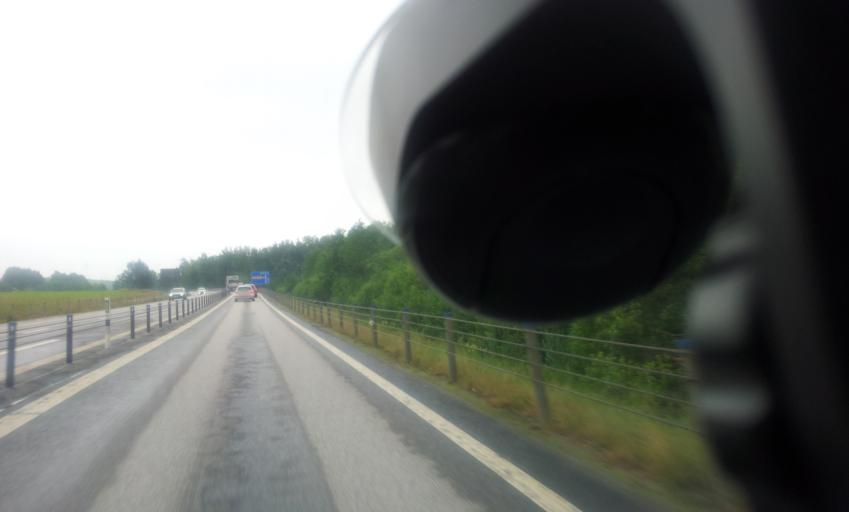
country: SE
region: Kalmar
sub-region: Vasterviks Kommun
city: Gamleby
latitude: 57.8093
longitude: 16.4943
